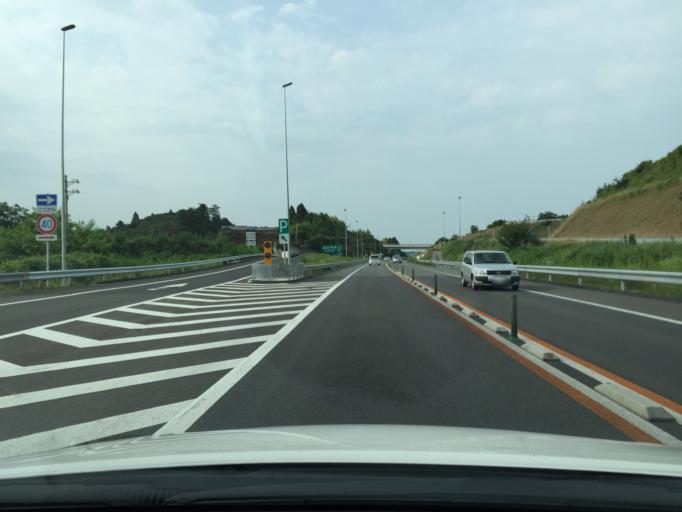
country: JP
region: Fukushima
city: Namie
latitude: 37.2854
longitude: 140.9815
